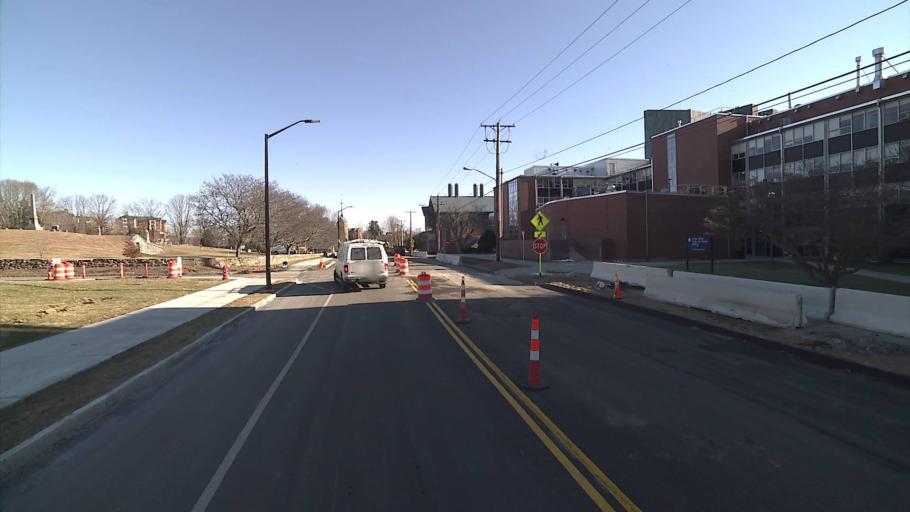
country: US
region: Connecticut
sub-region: Tolland County
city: Storrs
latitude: 41.8107
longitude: -72.2567
